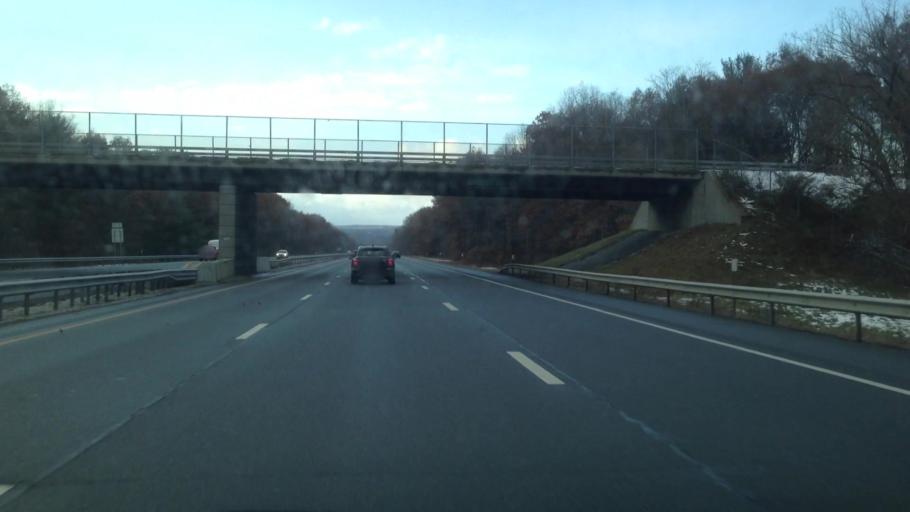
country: US
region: New York
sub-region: Schenectady County
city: Rotterdam
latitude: 42.7671
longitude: -73.9614
